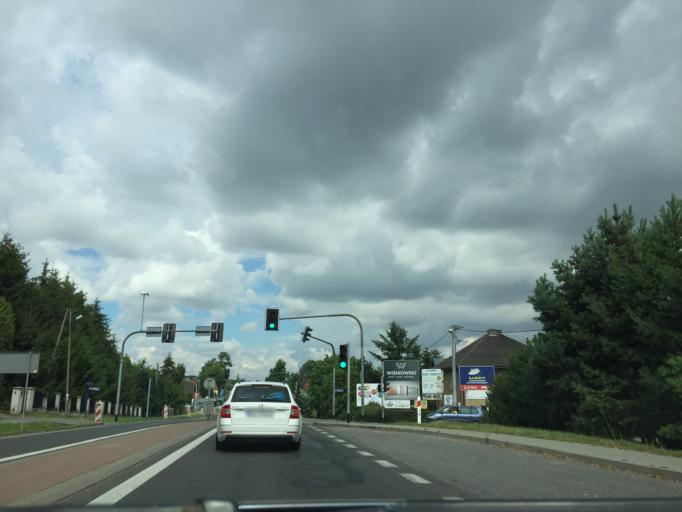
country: PL
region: Lesser Poland Voivodeship
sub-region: Powiat krakowski
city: Michalowice
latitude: 50.1589
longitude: 19.9804
